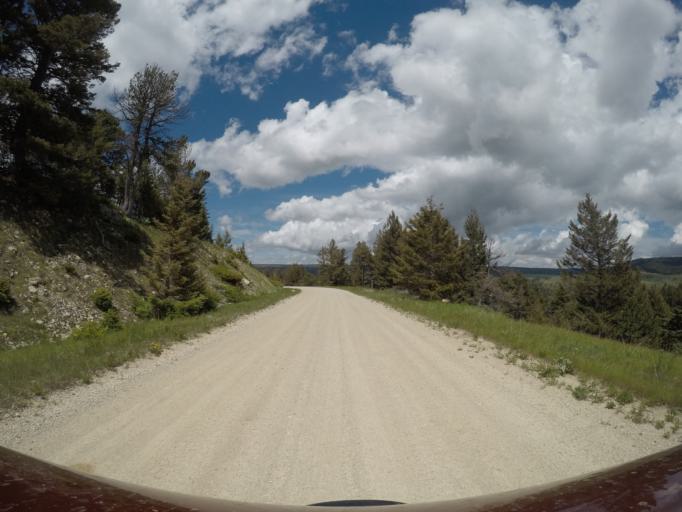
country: US
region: Wyoming
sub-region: Big Horn County
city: Lovell
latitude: 45.1938
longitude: -108.4832
